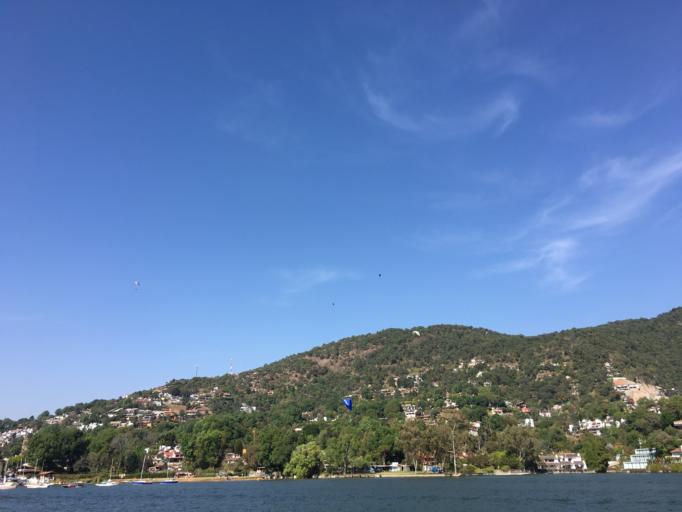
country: MX
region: Mexico
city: Valle de Bravo
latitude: 19.1808
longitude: -100.1287
